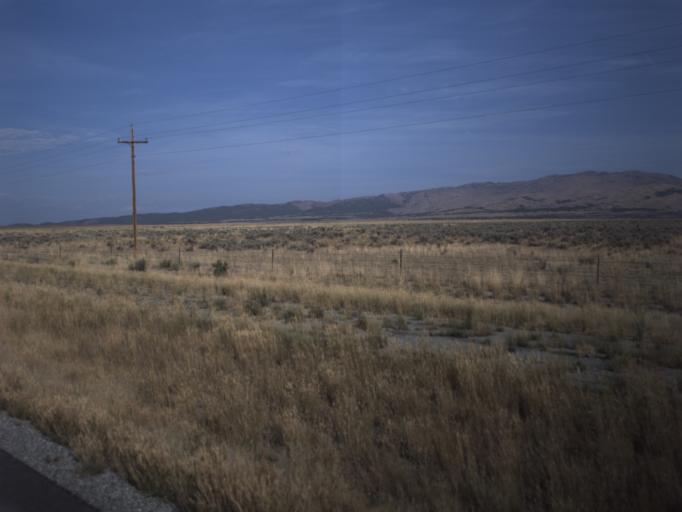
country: US
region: Idaho
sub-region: Oneida County
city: Malad City
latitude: 41.9657
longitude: -113.0091
